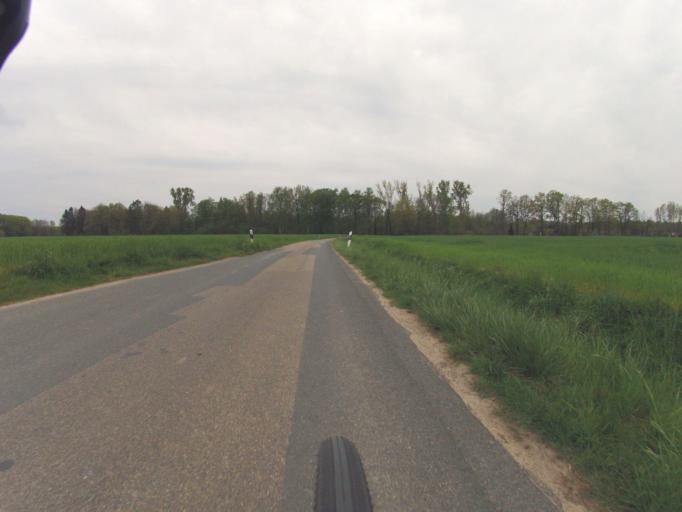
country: DE
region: North Rhine-Westphalia
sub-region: Regierungsbezirk Munster
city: Mettingen
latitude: 52.3154
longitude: 7.8237
